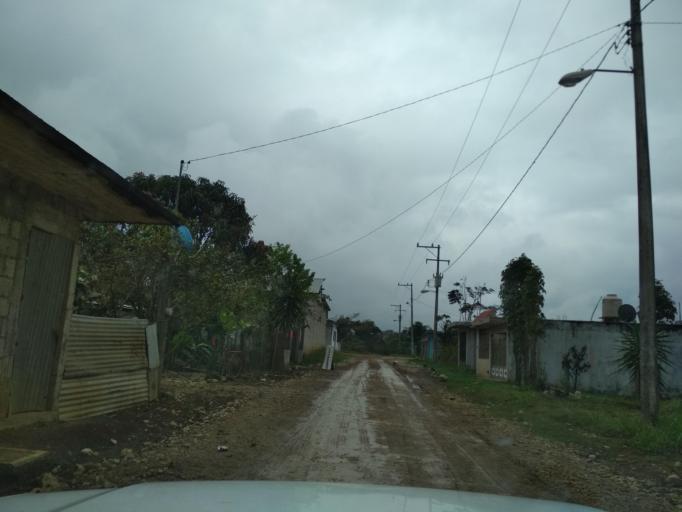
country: MX
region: Veracruz
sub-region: Cordoba
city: San Jose de Tapia
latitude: 18.8457
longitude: -96.9670
